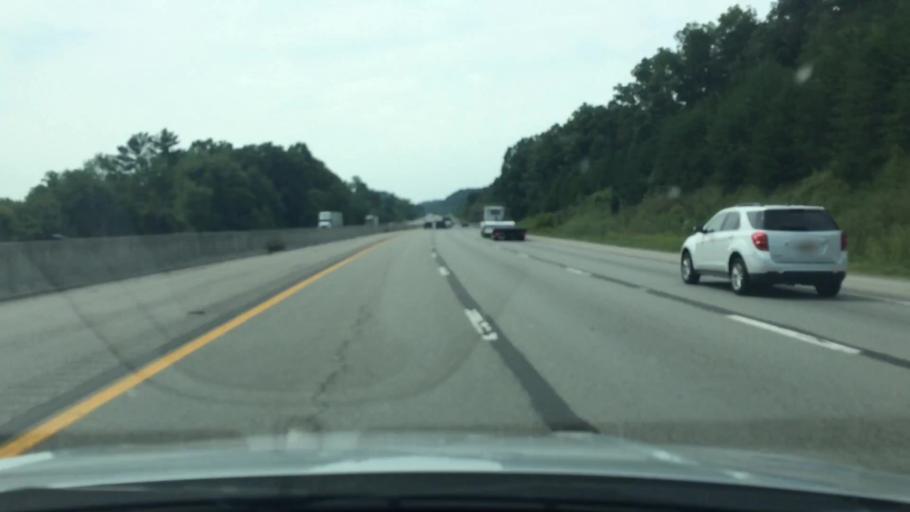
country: US
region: Kentucky
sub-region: Madison County
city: Berea
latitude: 37.5156
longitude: -84.3207
